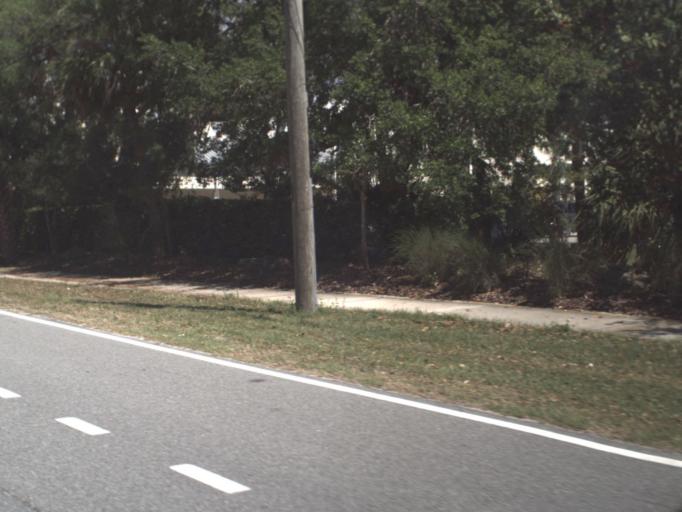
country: US
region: Florida
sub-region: Flagler County
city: Palm Coast
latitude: 29.6004
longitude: -81.1969
